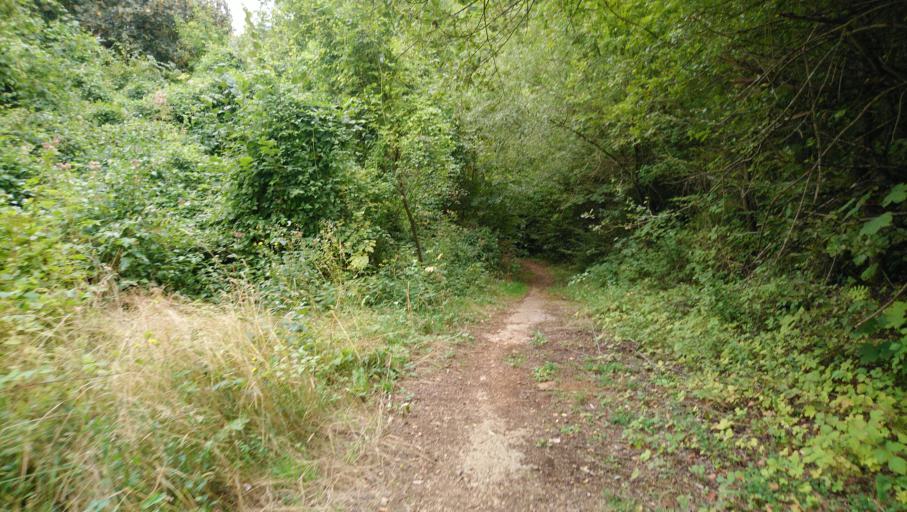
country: LU
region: Luxembourg
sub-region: Canton d'Esch-sur-Alzette
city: Obercorn
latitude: 49.5013
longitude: 5.9086
